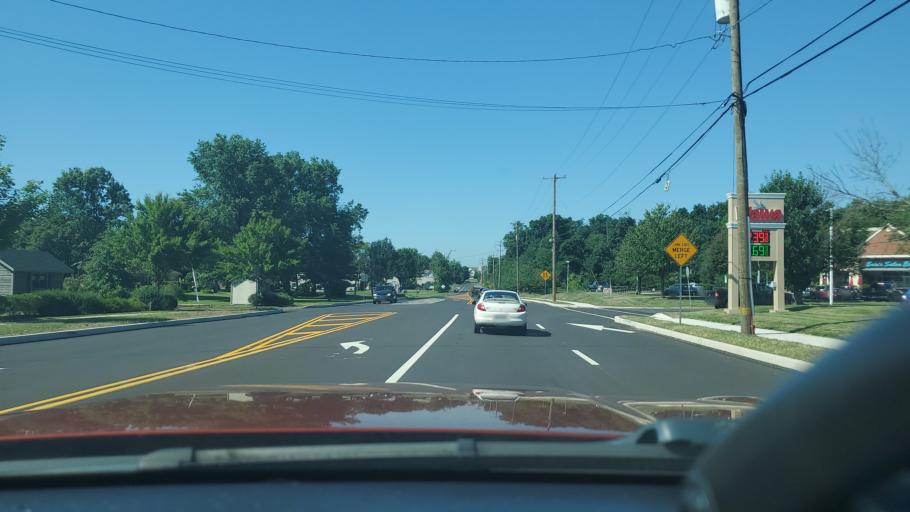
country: US
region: Pennsylvania
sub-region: Montgomery County
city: Limerick
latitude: 40.2321
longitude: -75.5279
